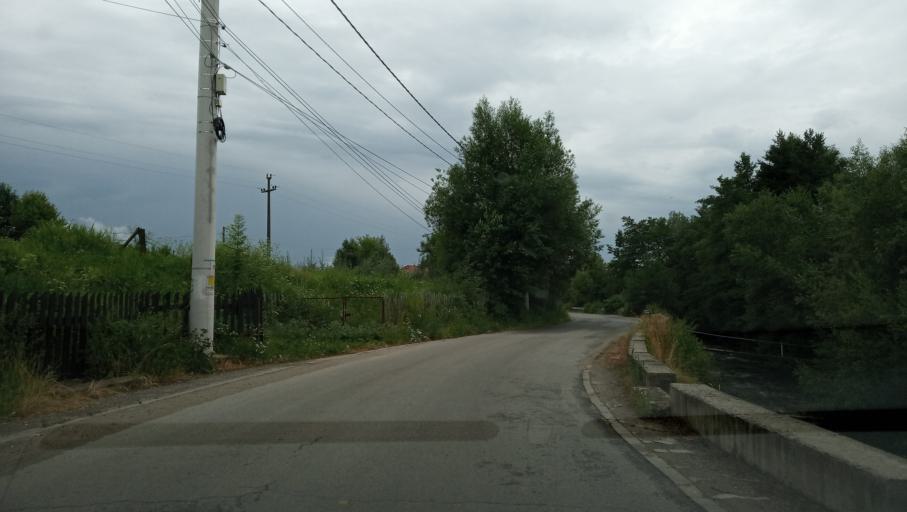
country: RO
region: Hunedoara
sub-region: Oras Petrila
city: Petrila
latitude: 45.4572
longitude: 23.4186
